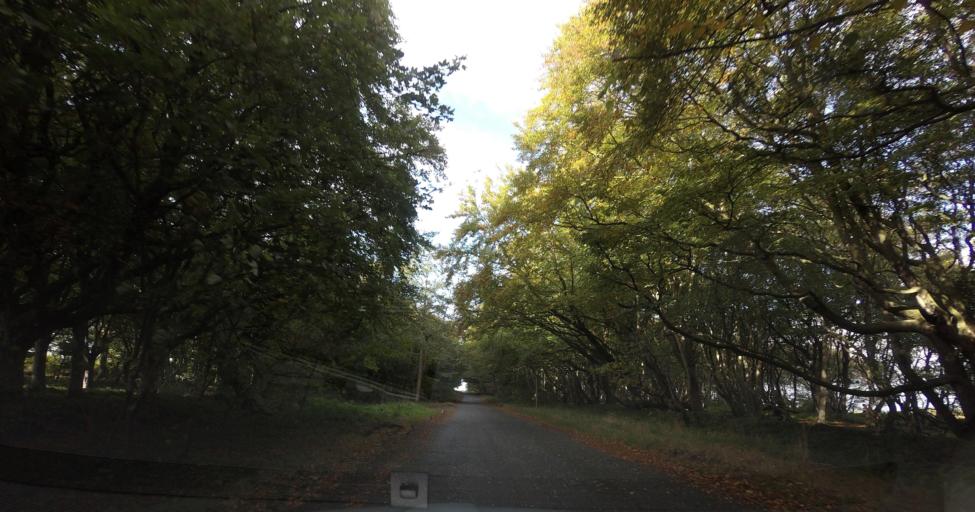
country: GB
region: Scotland
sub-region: Aberdeenshire
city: Whitehills
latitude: 57.6703
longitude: -2.5804
